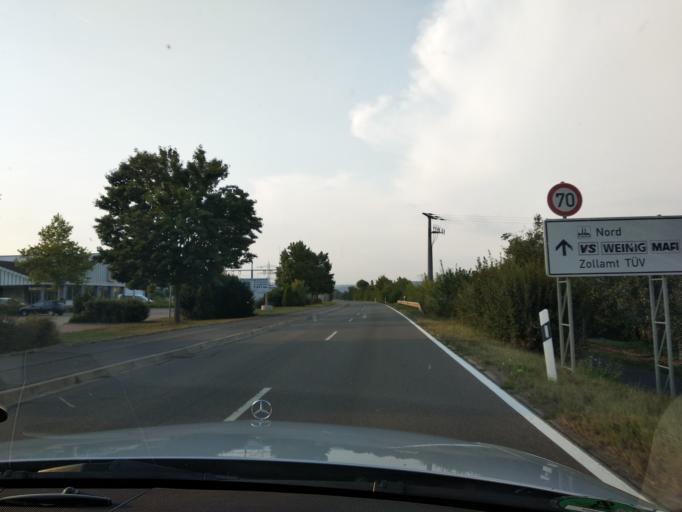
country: DE
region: Baden-Wuerttemberg
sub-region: Regierungsbezirk Stuttgart
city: Tauberbischofsheim
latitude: 49.6349
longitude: 9.6558
